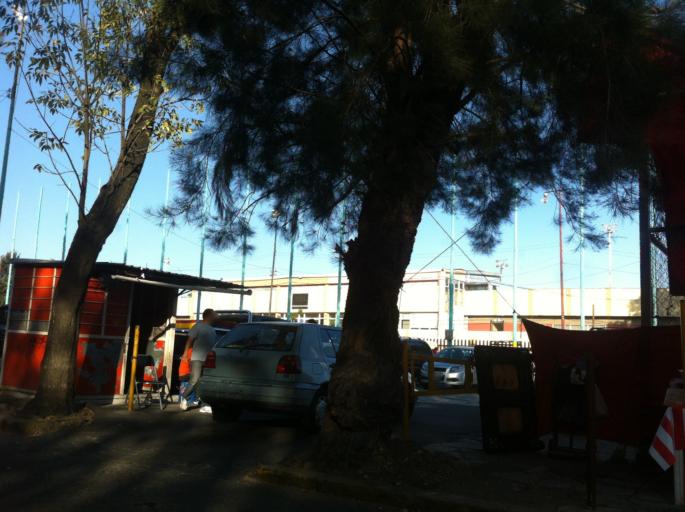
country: MX
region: Mexico City
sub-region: Iztacalco
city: Iztacalco
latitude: 19.4094
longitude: -99.1045
